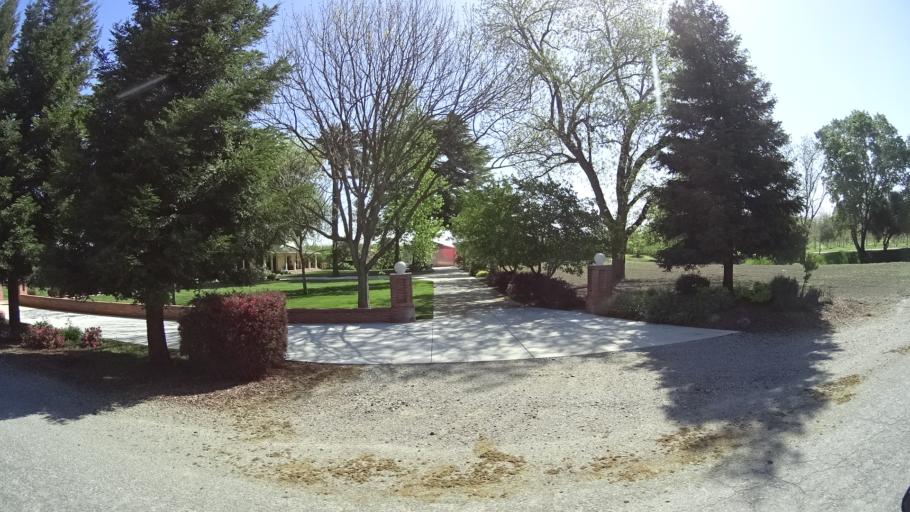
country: US
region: California
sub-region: Glenn County
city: Hamilton City
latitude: 39.7255
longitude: -122.0214
